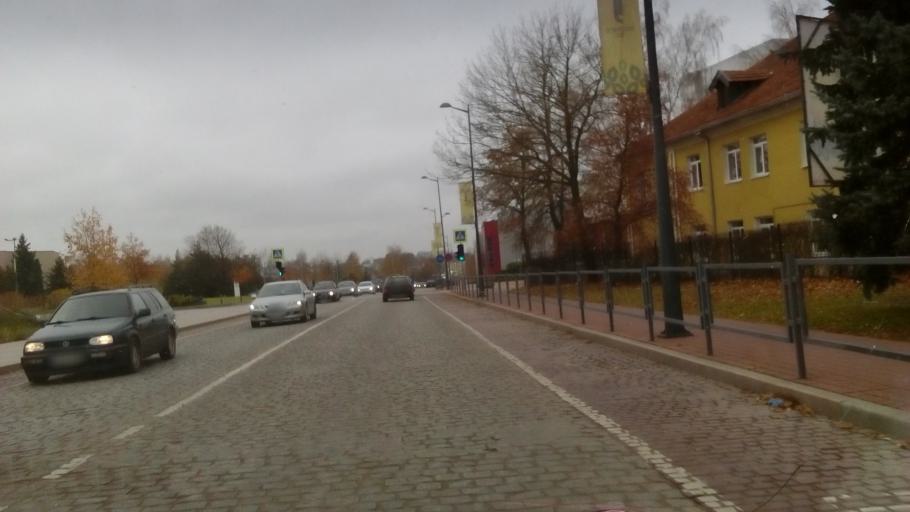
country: LT
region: Marijampoles apskritis
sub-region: Marijampole Municipality
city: Marijampole
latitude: 54.5577
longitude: 23.3511
